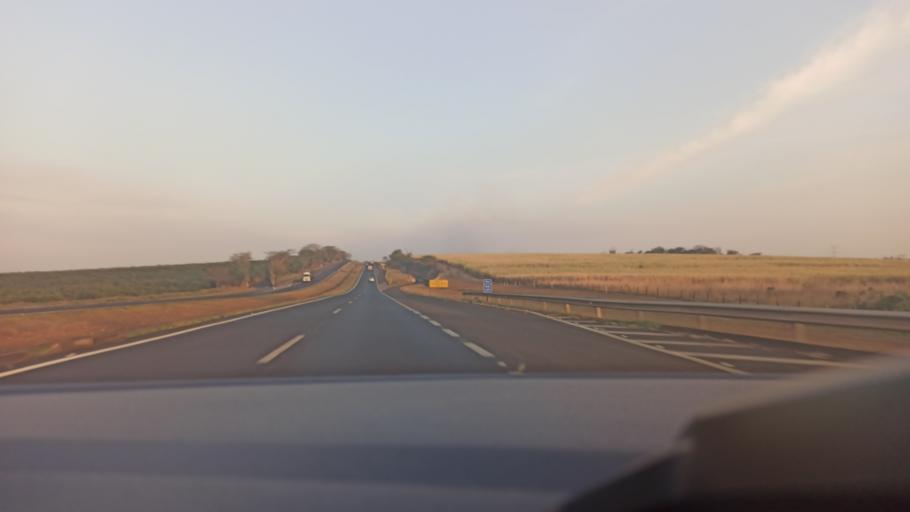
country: BR
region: Sao Paulo
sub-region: Taquaritinga
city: Taquaritinga
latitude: -21.4341
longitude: -48.6588
